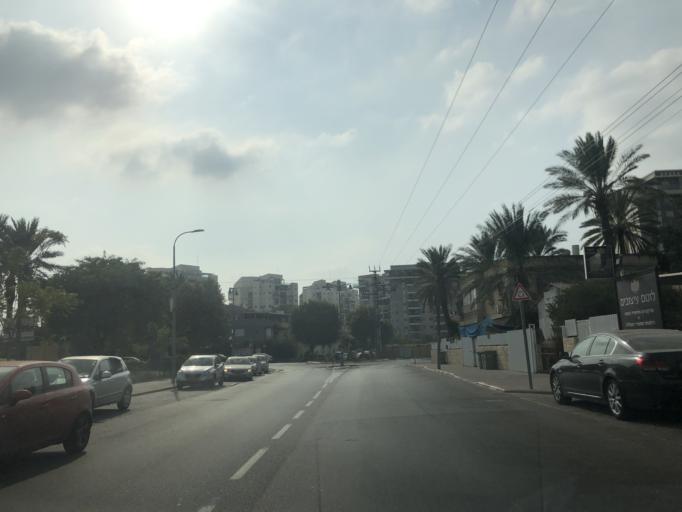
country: IL
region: Central District
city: Rosh Ha'Ayin
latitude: 32.0981
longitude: 34.9434
